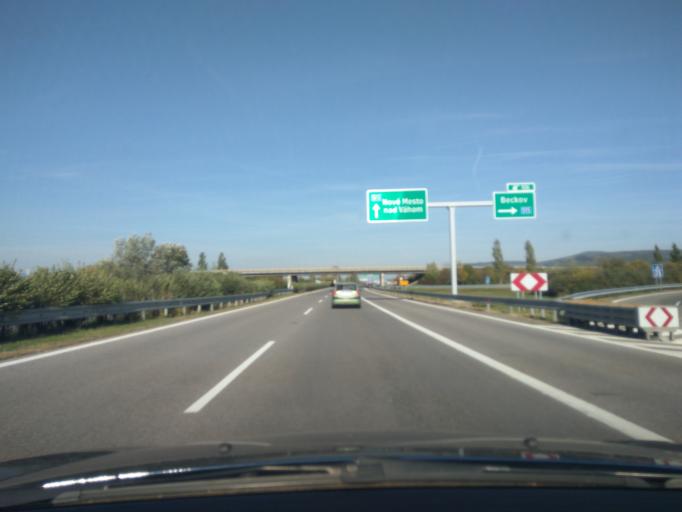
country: SK
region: Trenciansky
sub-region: Okres Nove Mesto nad Vahom
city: Nove Mesto nad Vahom
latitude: 48.7603
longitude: 17.8661
